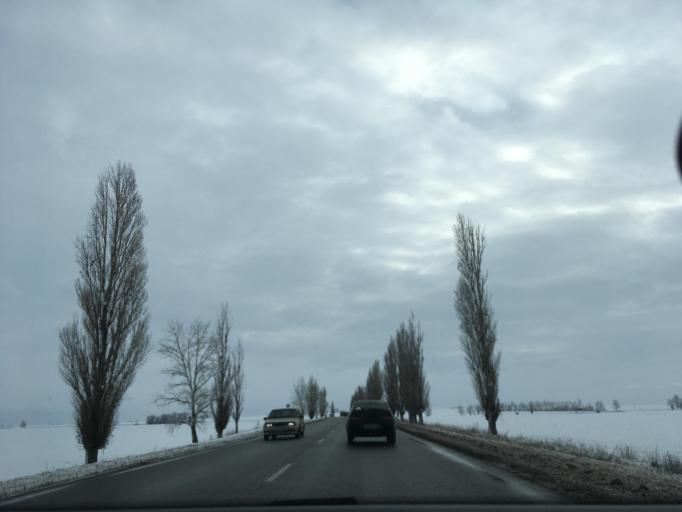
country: UA
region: Luhansk
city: Lozno-Oleksandrivka
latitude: 49.9563
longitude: 38.9488
